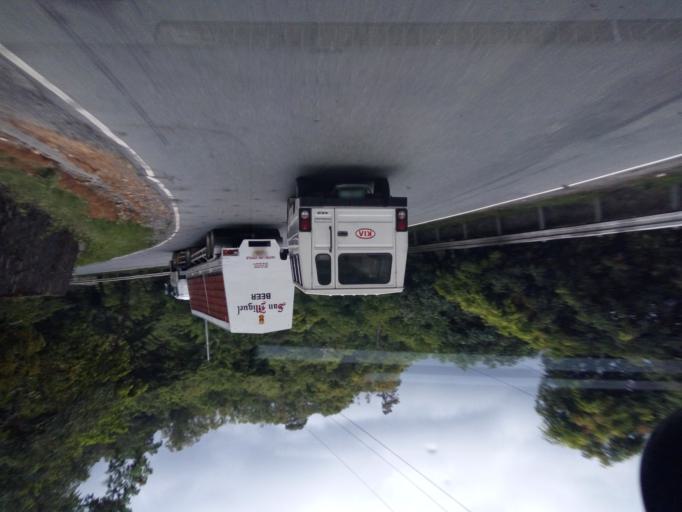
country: PH
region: Cagayan Valley
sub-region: Province of Nueva Vizcaya
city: Santa Fe
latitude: 16.1076
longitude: 120.9272
